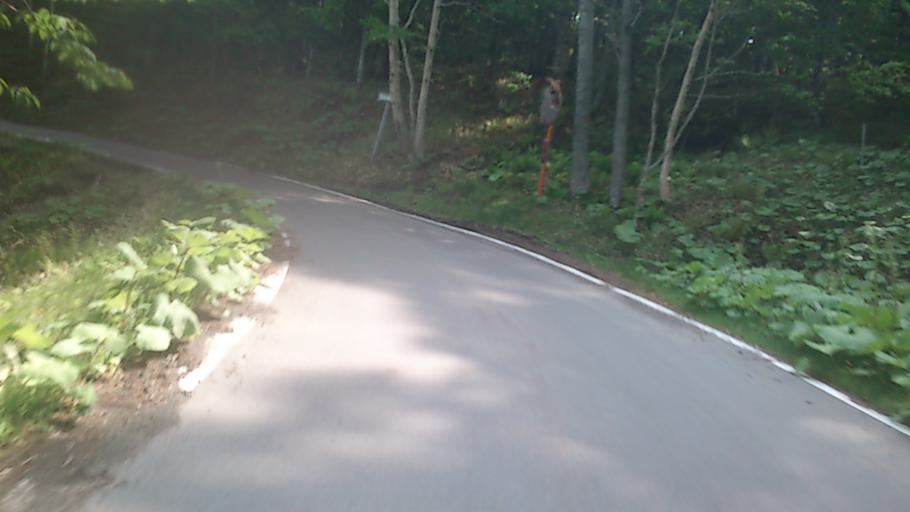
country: JP
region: Hokkaido
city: Kitami
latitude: 43.3833
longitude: 143.9655
